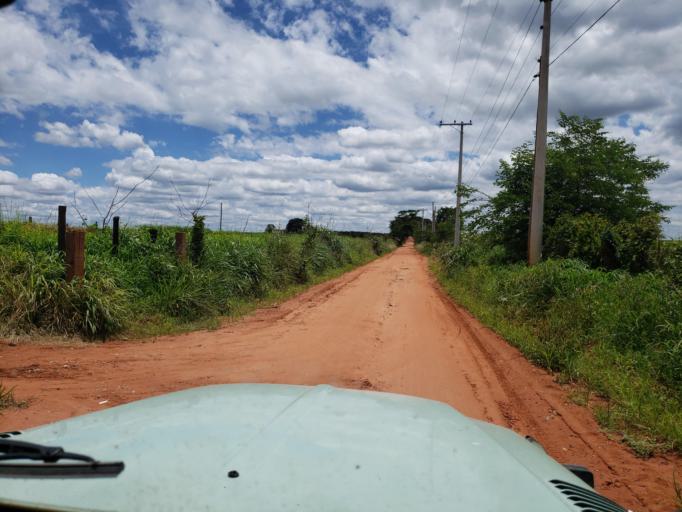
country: BR
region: Sao Paulo
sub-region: Aguai
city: Aguai
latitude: -22.1990
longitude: -46.9572
